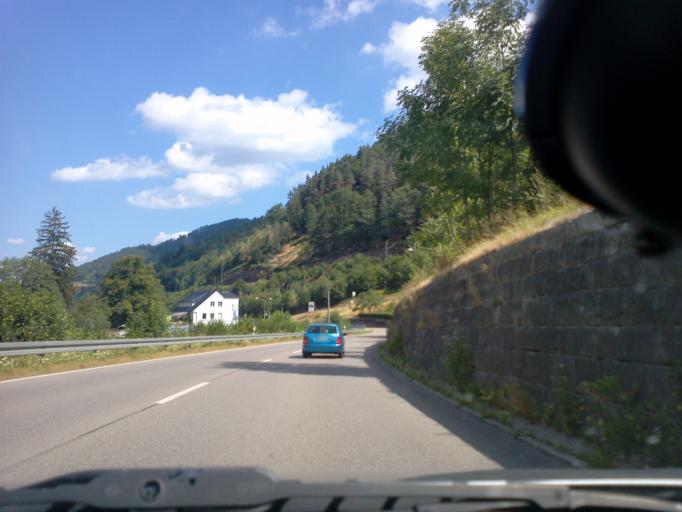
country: DE
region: Baden-Wuerttemberg
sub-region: Freiburg Region
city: Hornberg
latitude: 48.1994
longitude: 8.2348
